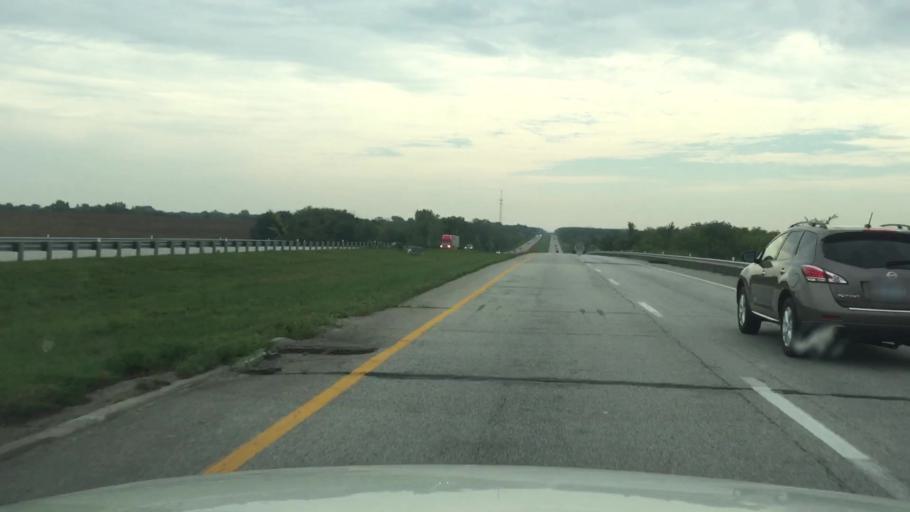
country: US
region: Missouri
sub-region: Clinton County
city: Lathrop
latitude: 39.5127
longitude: -94.2877
